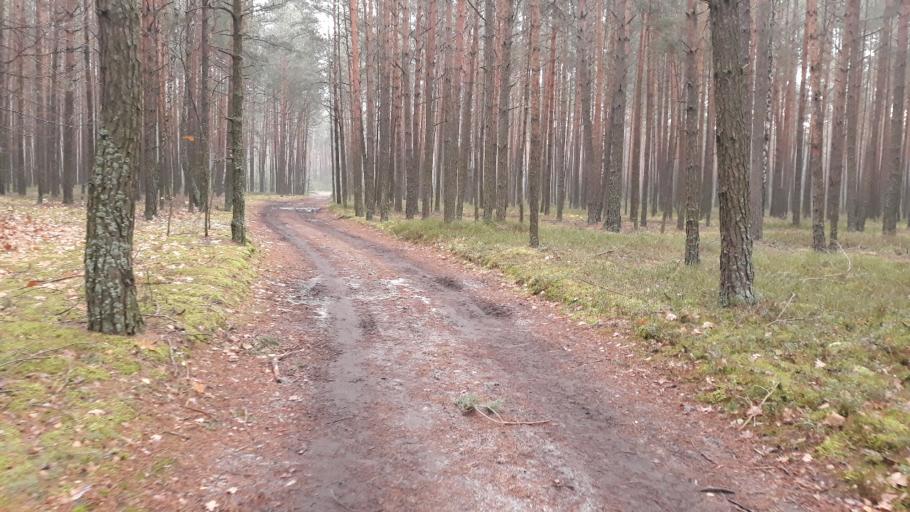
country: PL
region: Lublin Voivodeship
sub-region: Powiat janowski
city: Dzwola
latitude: 50.6447
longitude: 22.5827
